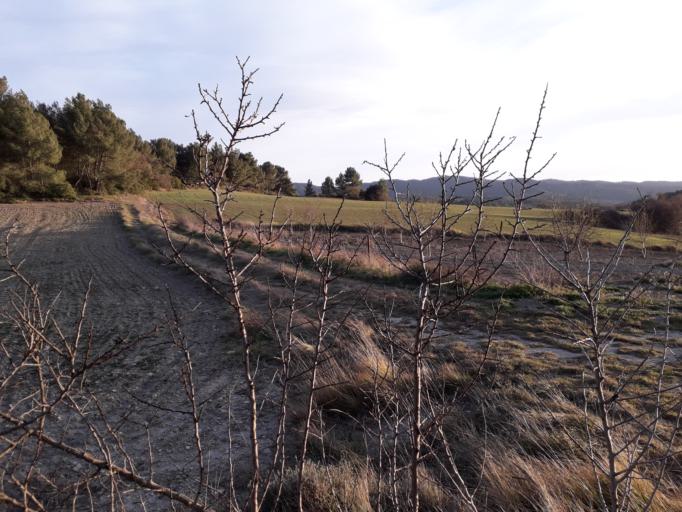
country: ES
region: Catalonia
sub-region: Provincia de Barcelona
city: Sant Marti de Tous
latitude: 41.5622
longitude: 1.4893
